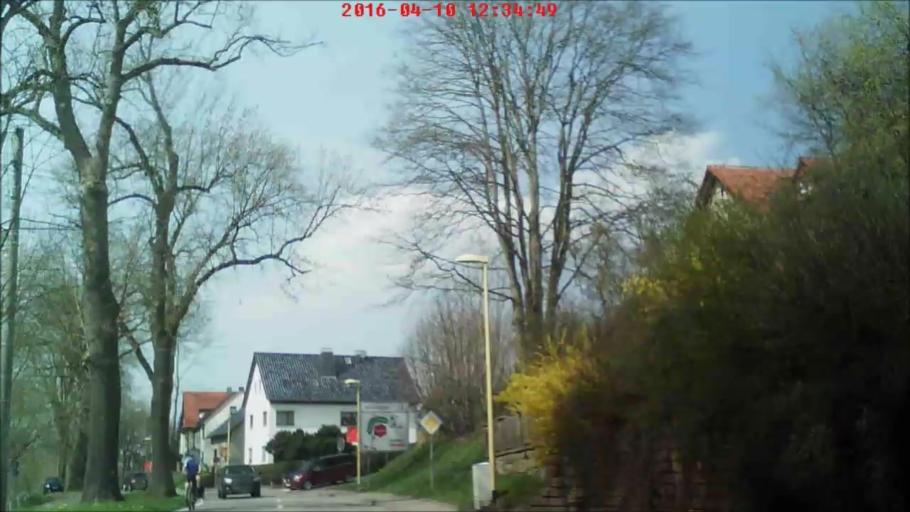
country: DE
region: Thuringia
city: Breitenbach
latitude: 50.7139
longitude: 10.4740
